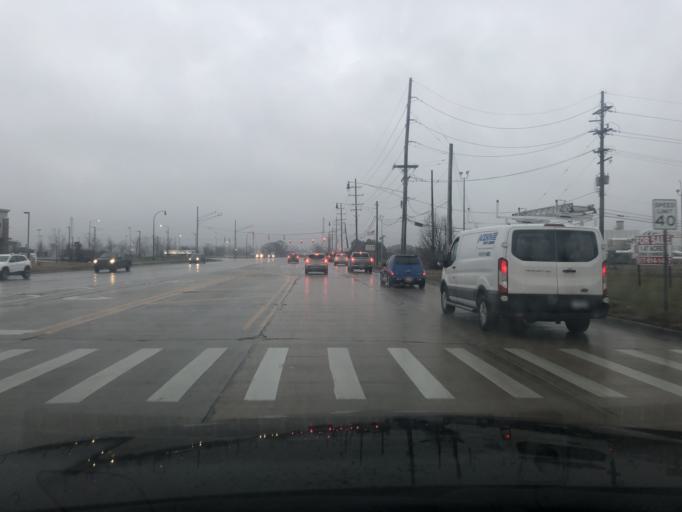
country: US
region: Michigan
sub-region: Wayne County
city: Woodhaven
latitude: 42.1393
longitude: -83.2371
